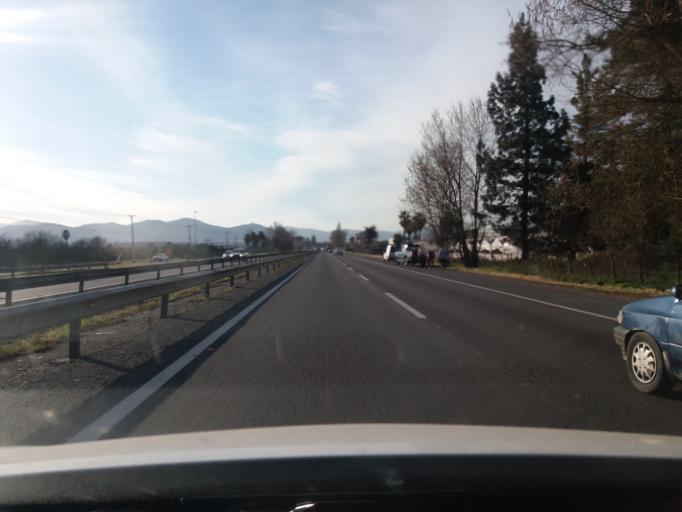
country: CL
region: Valparaiso
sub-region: Provincia de Quillota
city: Hacienda La Calera
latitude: -32.7981
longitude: -71.1582
